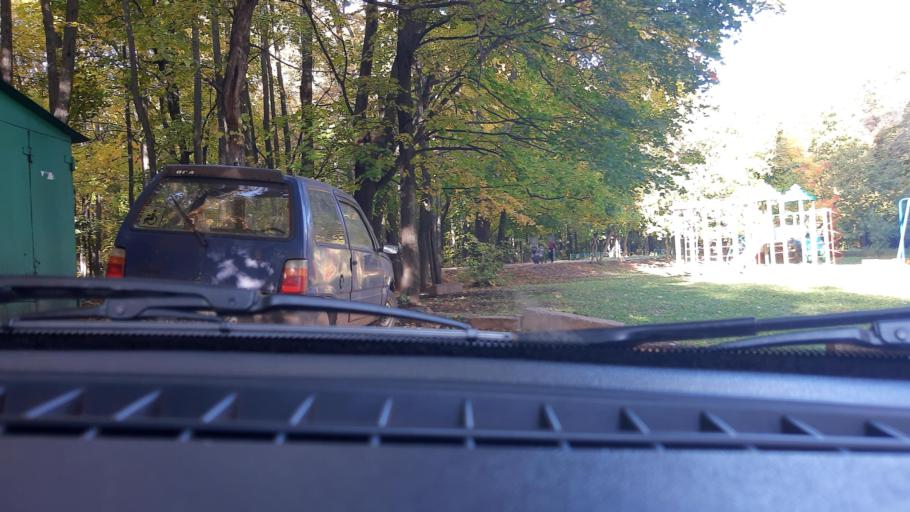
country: RU
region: Bashkortostan
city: Ufa
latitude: 54.7569
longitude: 55.9911
